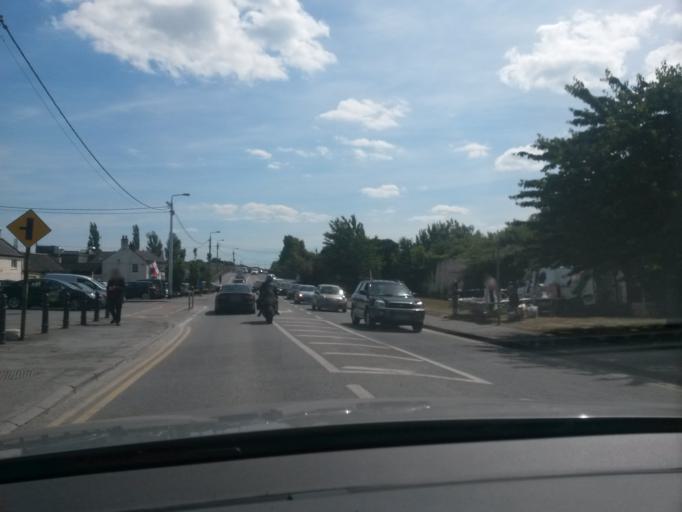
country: IE
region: Leinster
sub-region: Kildare
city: Sallins
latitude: 53.2505
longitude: -6.6653
